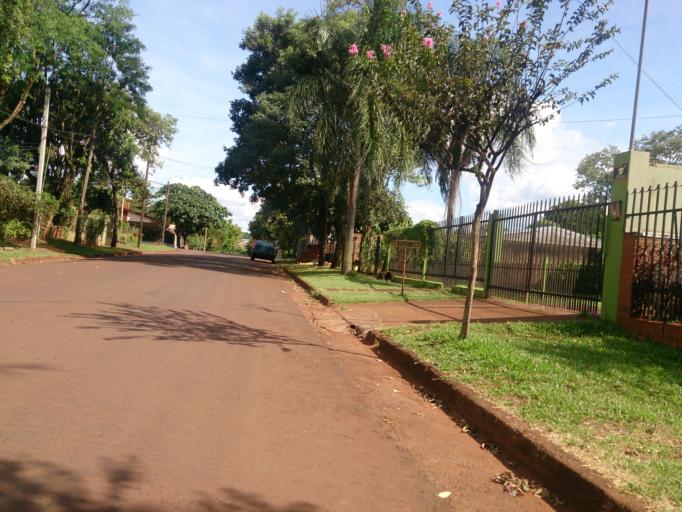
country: AR
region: Misiones
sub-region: Departamento de Obera
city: Obera
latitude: -27.4931
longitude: -55.1265
